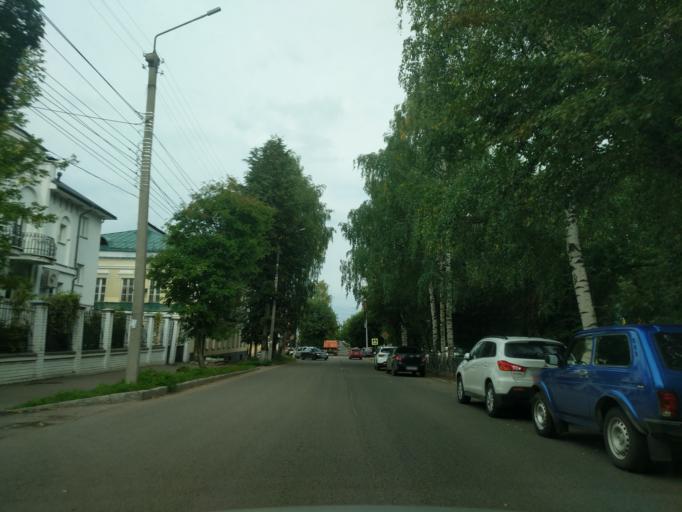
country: RU
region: Kirov
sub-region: Kirovo-Chepetskiy Rayon
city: Kirov
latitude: 58.5963
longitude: 49.6838
